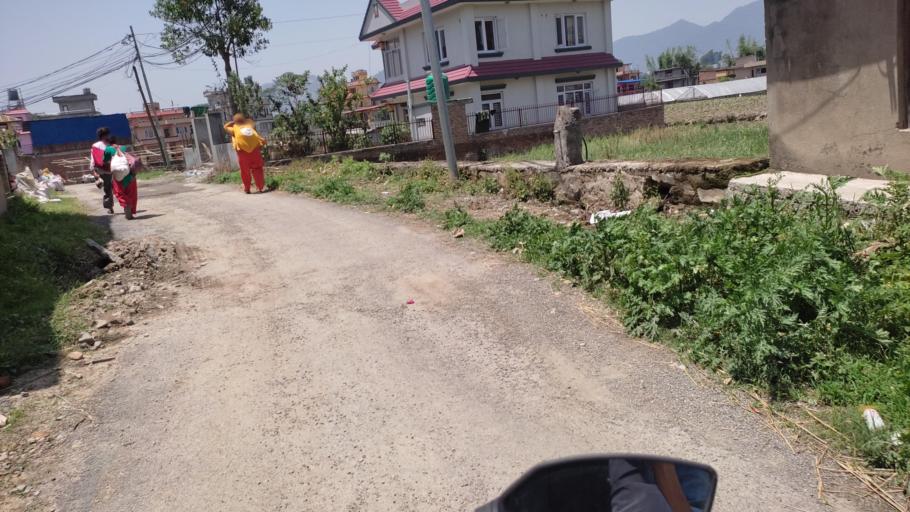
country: NP
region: Central Region
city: Kirtipur
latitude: 27.6743
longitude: 85.2669
